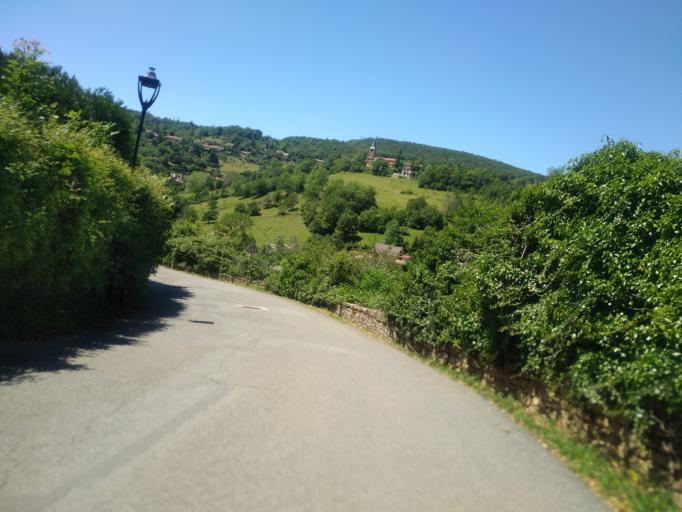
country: FR
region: Rhone-Alpes
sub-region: Departement du Rhone
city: Albigny-sur-Saone
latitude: 45.8556
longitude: 4.8089
